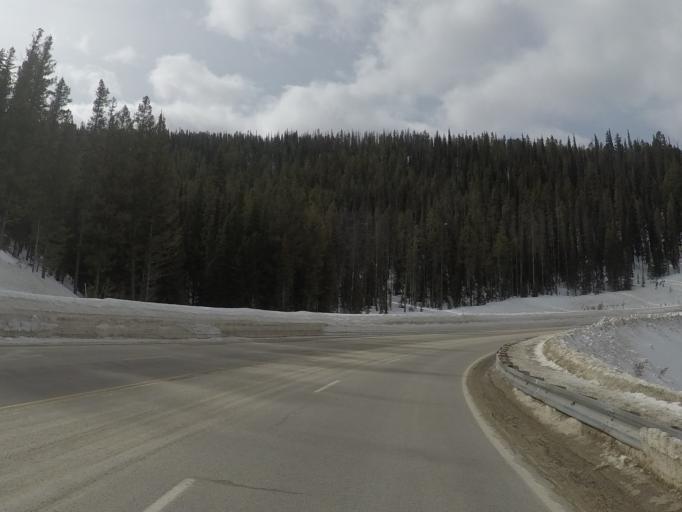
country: US
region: Idaho
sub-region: Lemhi County
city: Salmon
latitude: 45.7053
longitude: -113.9339
